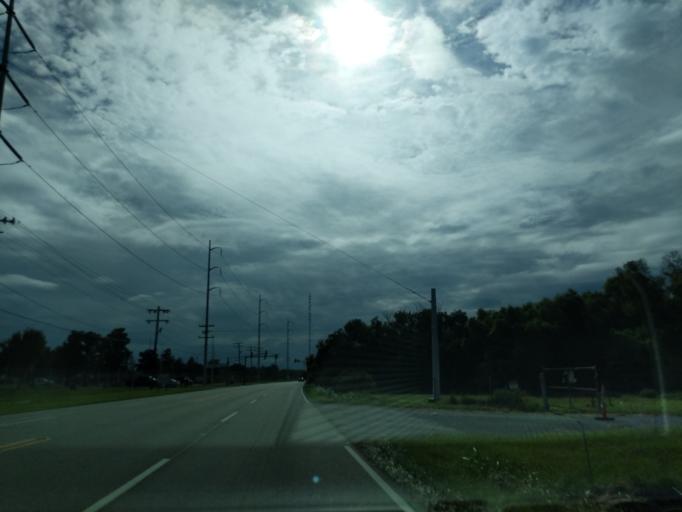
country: US
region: Louisiana
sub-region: Saint Bernard Parish
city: Chalmette
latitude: 30.0249
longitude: -89.9197
